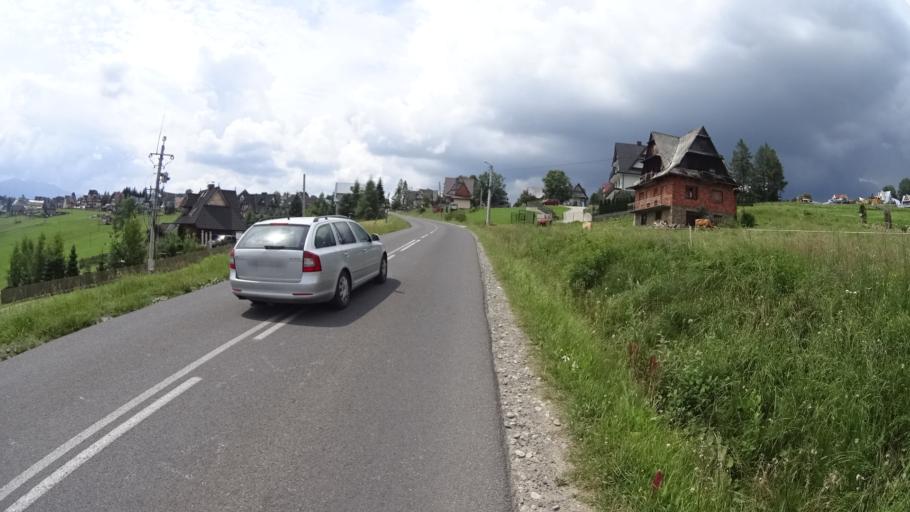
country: PL
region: Lesser Poland Voivodeship
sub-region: Powiat tatrzanski
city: Zakopane
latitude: 49.3392
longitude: 19.9534
